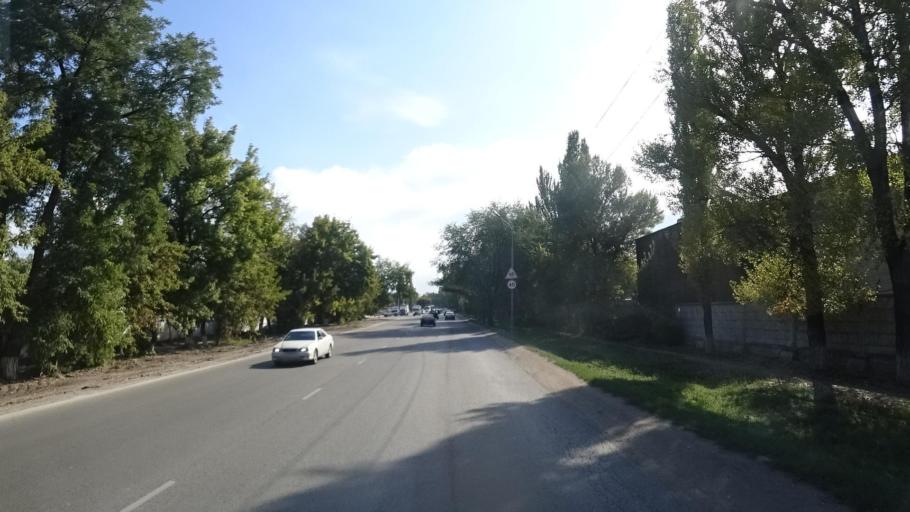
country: KZ
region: Almaty Oblysy
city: Energeticheskiy
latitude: 43.3825
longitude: 76.9985
